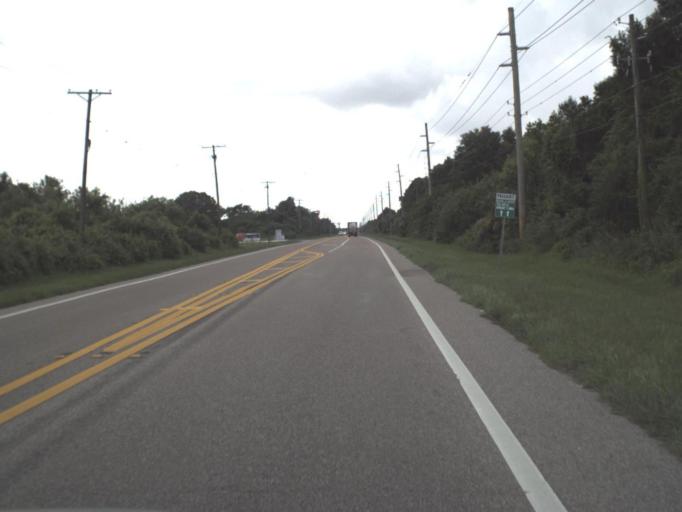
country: US
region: Florida
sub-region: Hillsborough County
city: Sun City Center
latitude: 27.7317
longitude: -82.3353
